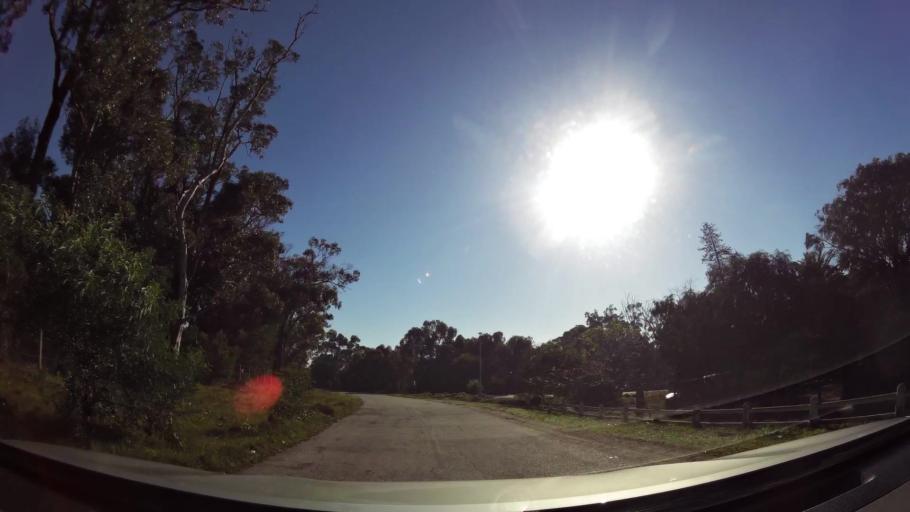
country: ZA
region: Eastern Cape
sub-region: Nelson Mandela Bay Metropolitan Municipality
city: Port Elizabeth
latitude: -33.9869
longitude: 25.6331
